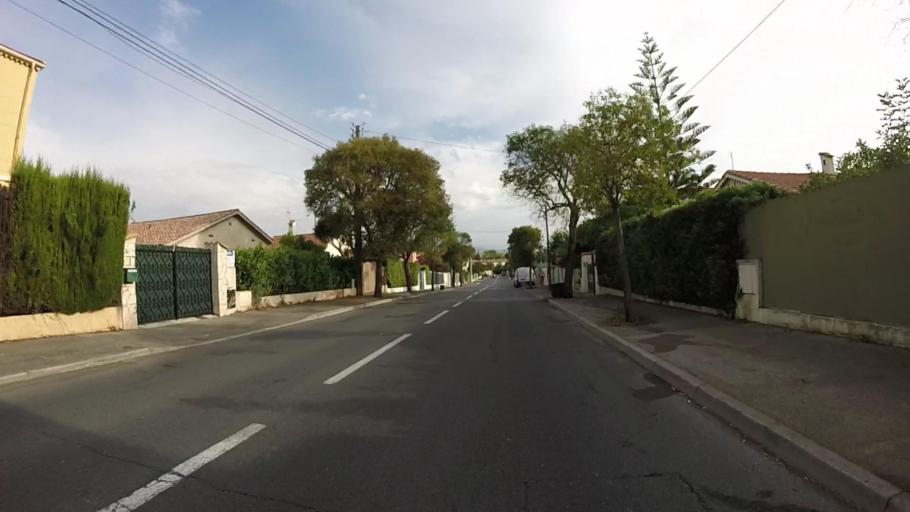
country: FR
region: Provence-Alpes-Cote d'Azur
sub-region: Departement des Alpes-Maritimes
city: Antibes
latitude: 43.5856
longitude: 7.1072
